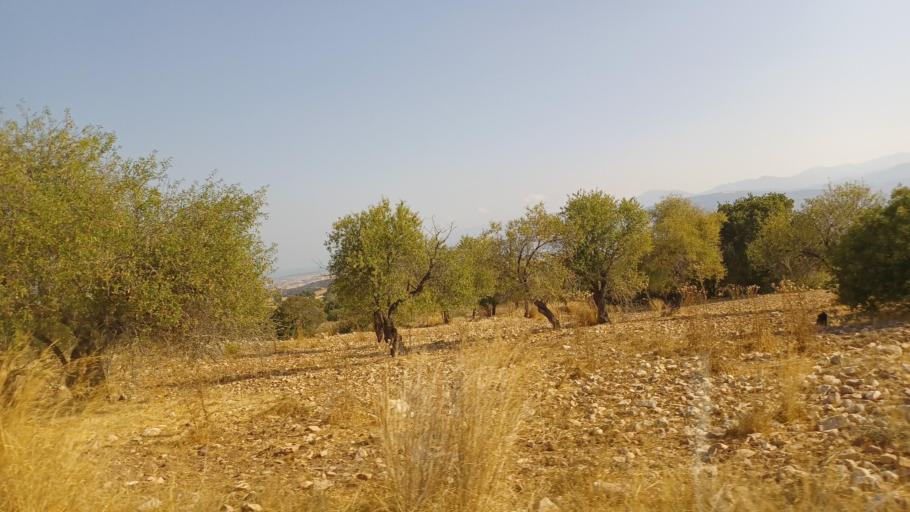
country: CY
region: Pafos
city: Polis
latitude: 34.9703
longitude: 32.4219
